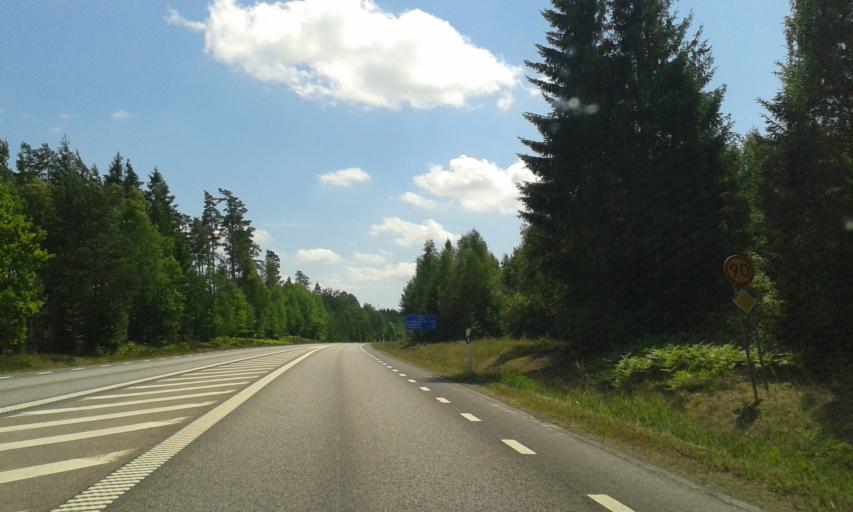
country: SE
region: Kronoberg
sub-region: Vaxjo Kommun
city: Ingelstad
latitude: 56.8083
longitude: 14.8864
